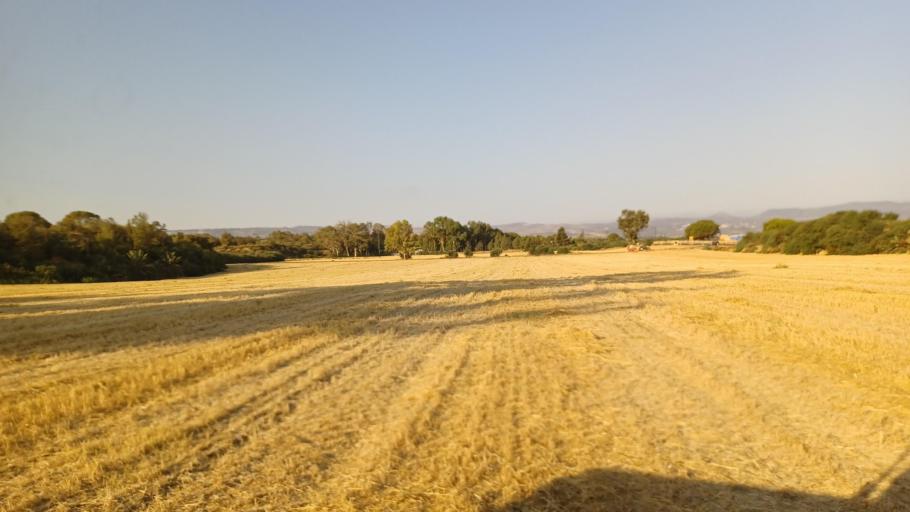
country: CY
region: Pafos
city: Polis
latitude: 35.0589
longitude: 32.4591
